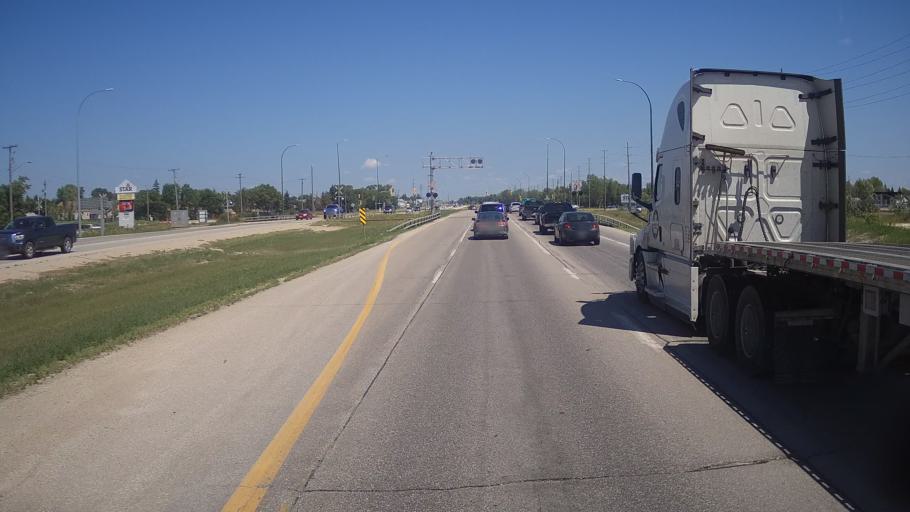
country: CA
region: Manitoba
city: Winnipeg
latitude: 49.9292
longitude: -97.0463
